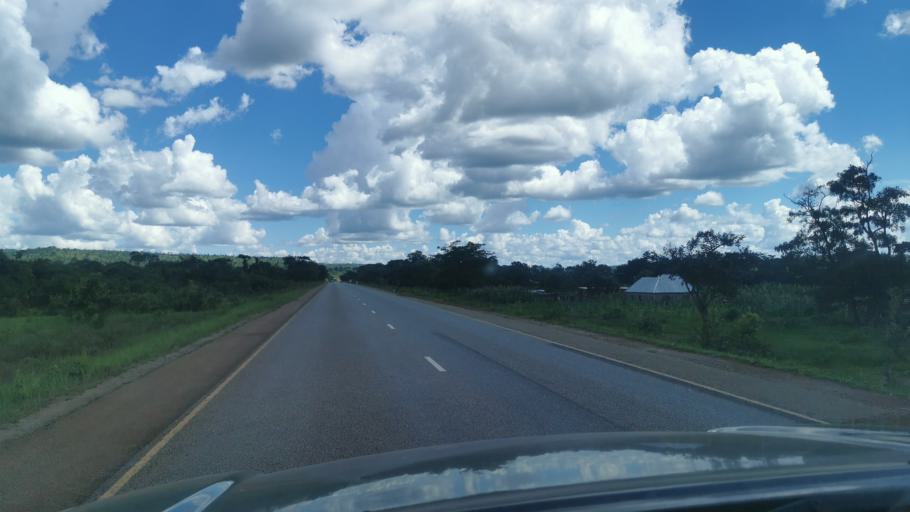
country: TZ
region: Geita
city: Uyovu
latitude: -3.0943
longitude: 31.2991
